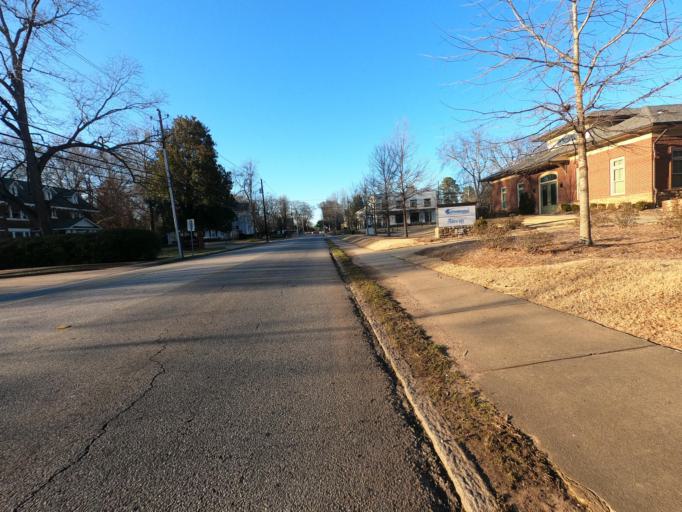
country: US
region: Georgia
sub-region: Clarke County
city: Athens
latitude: 33.9577
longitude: -83.3892
